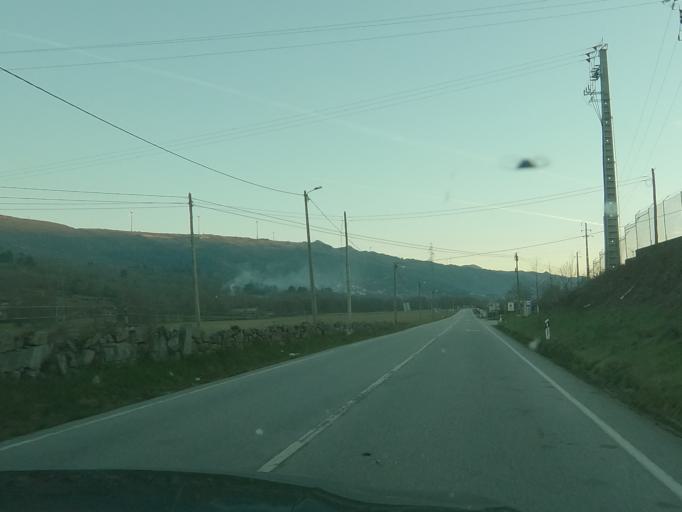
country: PT
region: Vila Real
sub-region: Vila Pouca de Aguiar
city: Vila Pouca de Aguiar
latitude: 41.4642
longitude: -7.6653
